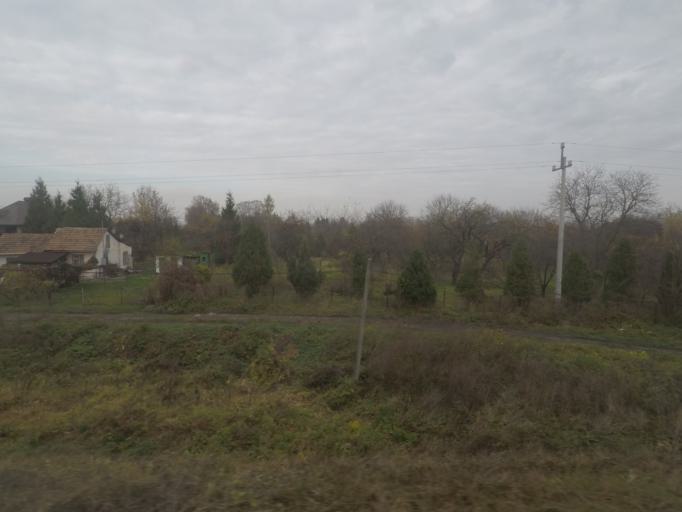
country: PL
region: Subcarpathian Voivodeship
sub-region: Powiat przemyski
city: Zurawica
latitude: 49.7842
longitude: 22.8229
